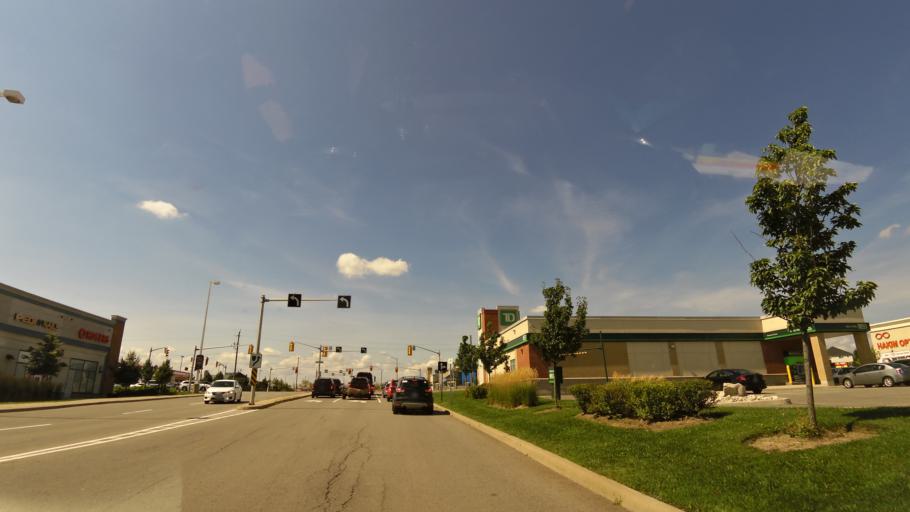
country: CA
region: Ontario
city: Hamilton
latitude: 43.3172
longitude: -79.9103
